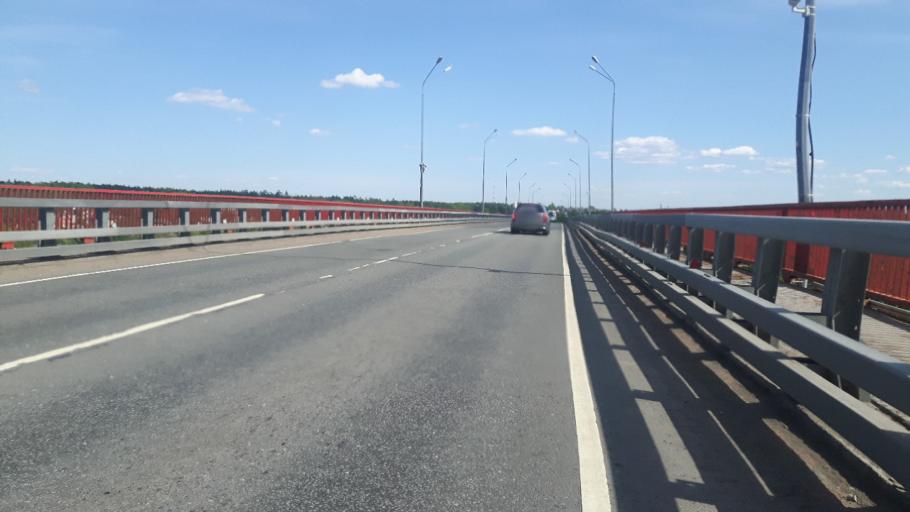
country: RU
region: Leningrad
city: Vyborg
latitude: 60.7376
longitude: 28.6892
